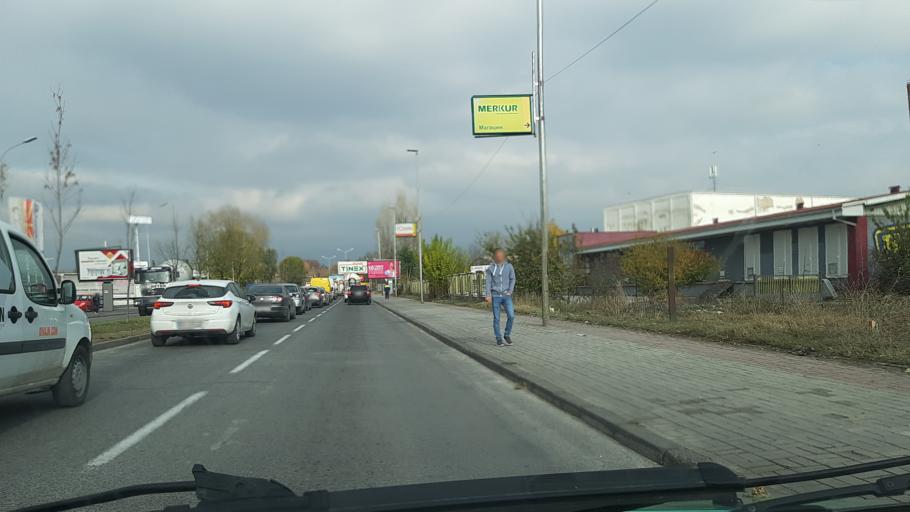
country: MK
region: Kisela Voda
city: Usje
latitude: 41.9946
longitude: 21.4757
